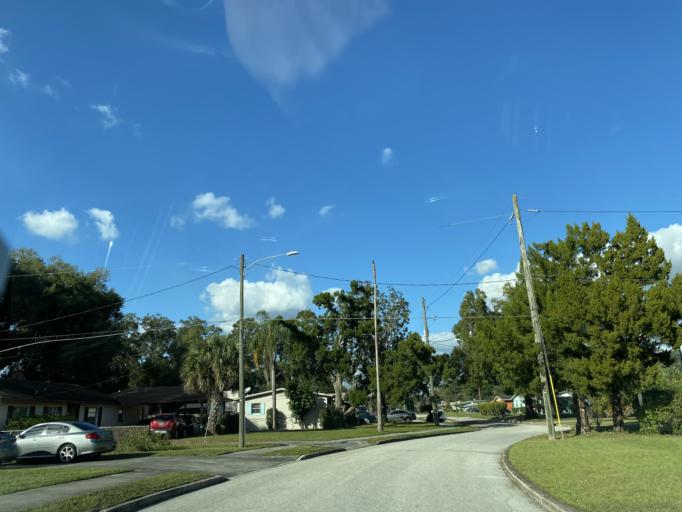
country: US
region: Florida
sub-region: Orange County
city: Orlando
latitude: 28.5479
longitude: -81.4049
